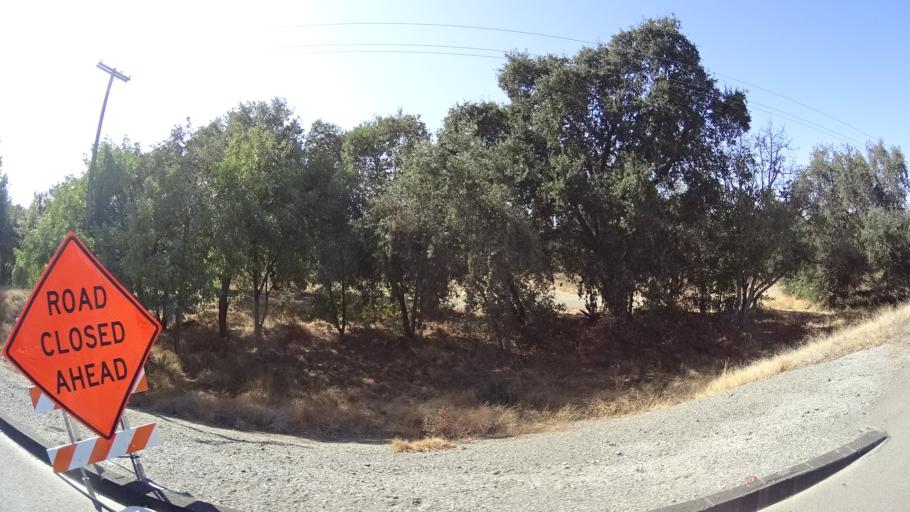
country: US
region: California
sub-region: Yolo County
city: West Sacramento
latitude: 38.6091
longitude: -121.5605
